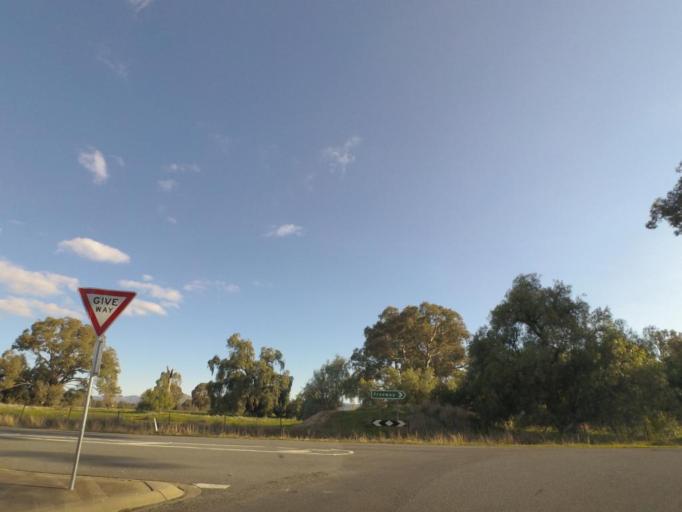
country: AU
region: Victoria
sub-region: Benalla
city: Benalla
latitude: -36.6967
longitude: 145.6585
